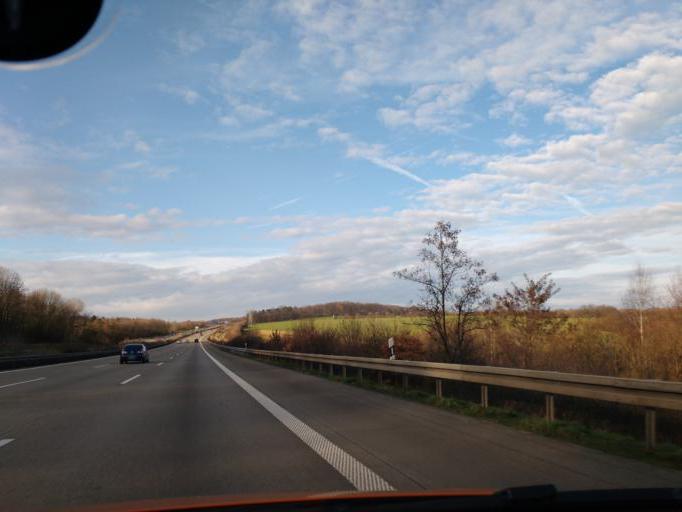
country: DE
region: Saxony-Anhalt
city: Beendorf
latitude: 52.2109
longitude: 11.1053
